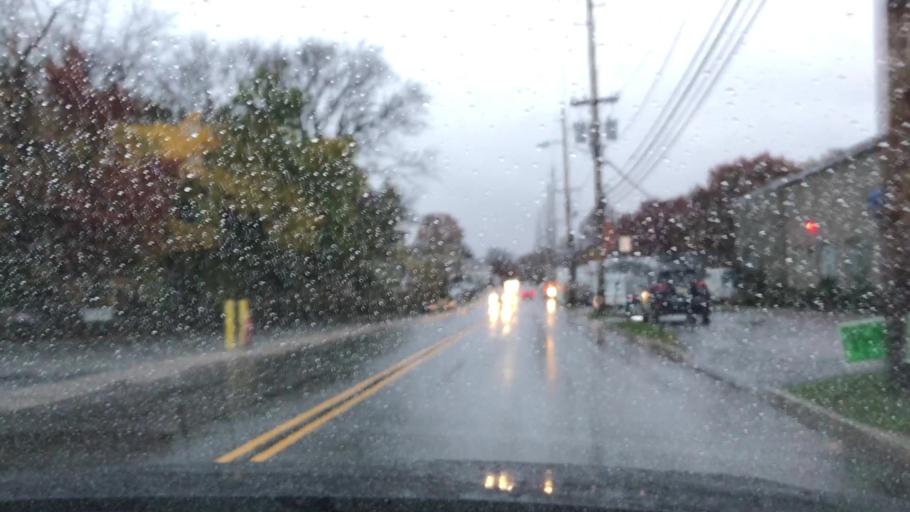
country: US
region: New Jersey
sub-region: Bergen County
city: Bergenfield
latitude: 40.9176
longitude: -74.0004
